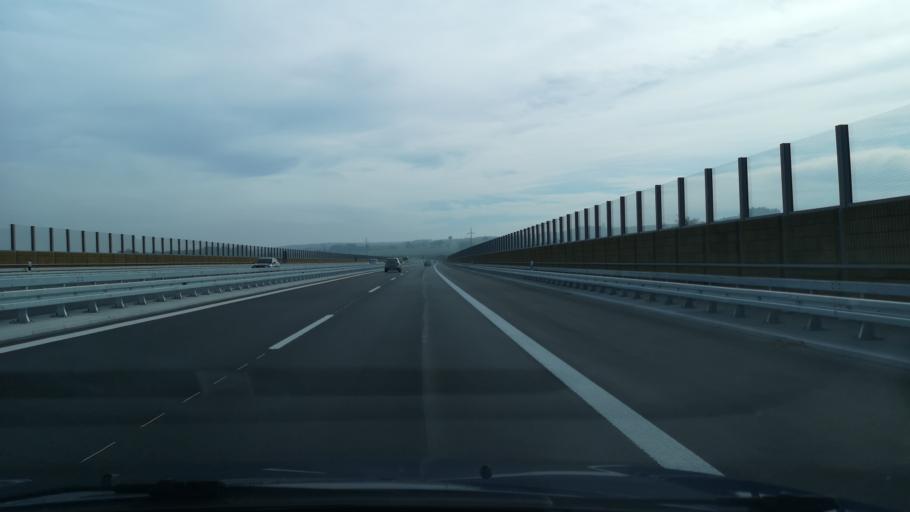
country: DE
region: Bavaria
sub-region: Upper Bavaria
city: Dorfen
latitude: 48.2568
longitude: 12.1935
